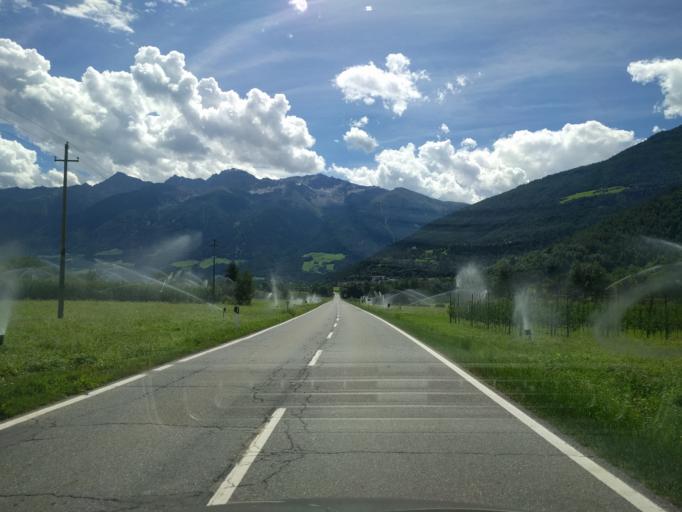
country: IT
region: Trentino-Alto Adige
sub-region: Bolzano
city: Sluderno
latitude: 46.6482
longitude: 10.5675
